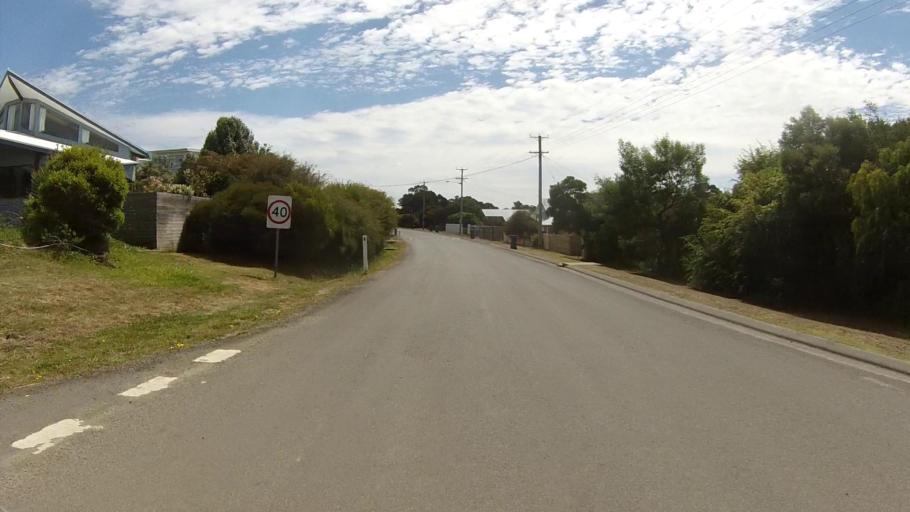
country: AU
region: Tasmania
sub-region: Clarence
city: Sandford
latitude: -42.9909
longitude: 147.5230
